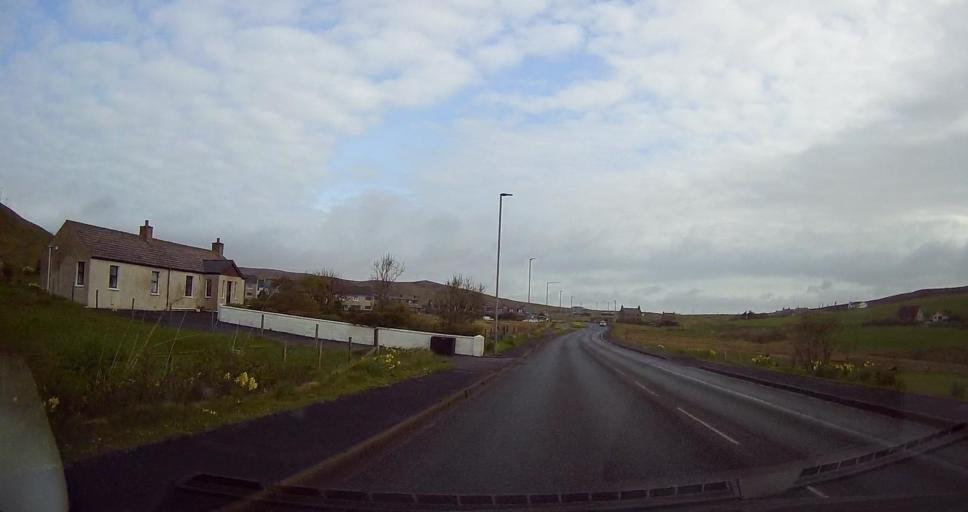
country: GB
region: Scotland
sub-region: Shetland Islands
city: Sandwick
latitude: 60.0509
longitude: -1.2266
